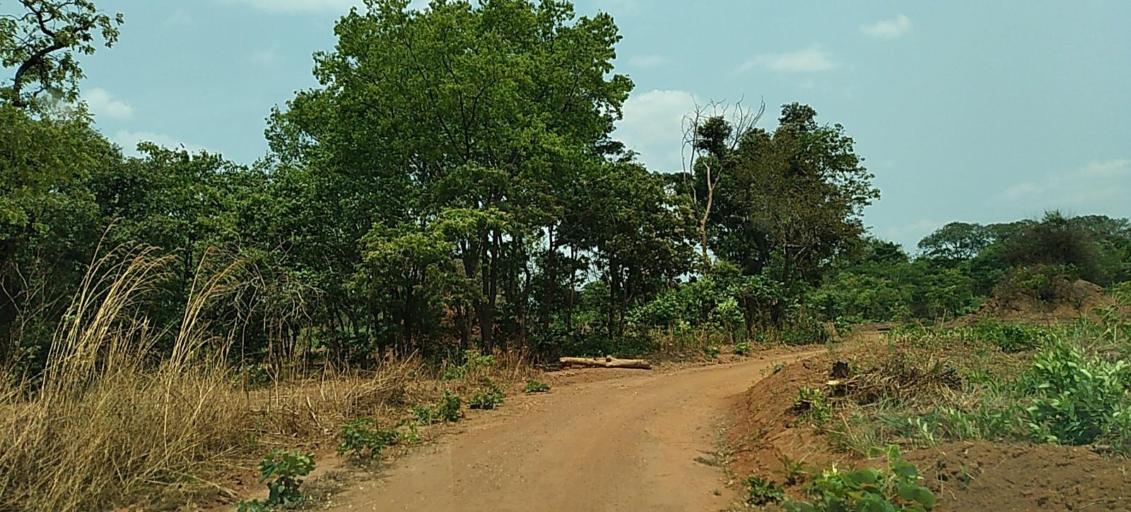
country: ZM
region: Copperbelt
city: Kalulushi
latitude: -12.7588
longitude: 28.0180
